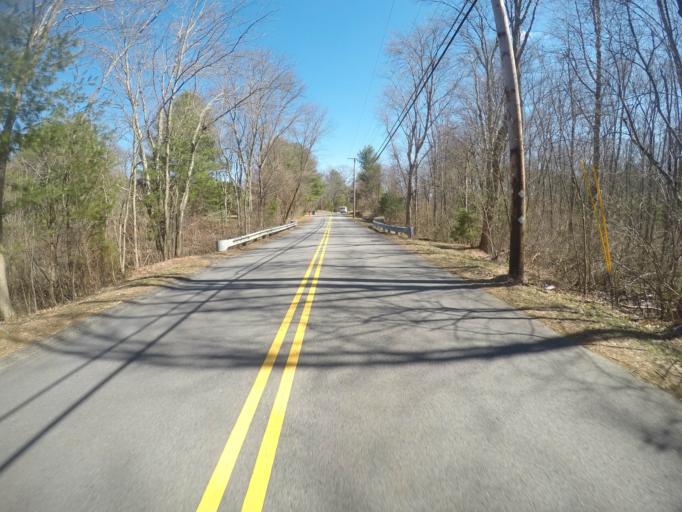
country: US
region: Massachusetts
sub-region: Bristol County
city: Easton
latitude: 42.0125
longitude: -71.1562
